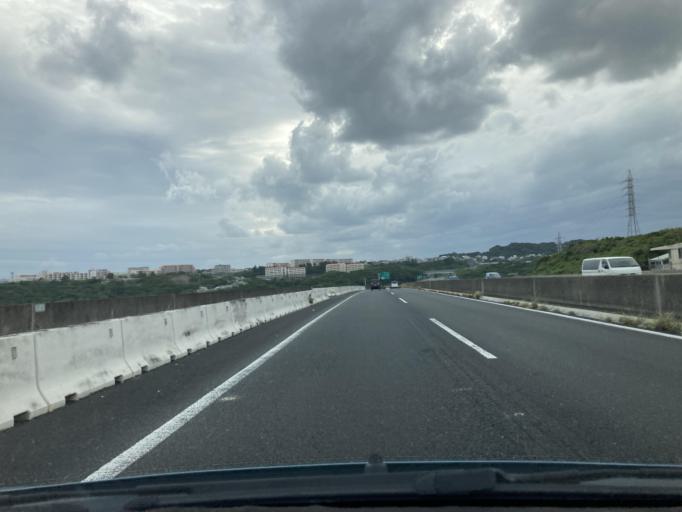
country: JP
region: Okinawa
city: Tomigusuku
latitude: 26.1751
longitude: 127.7059
